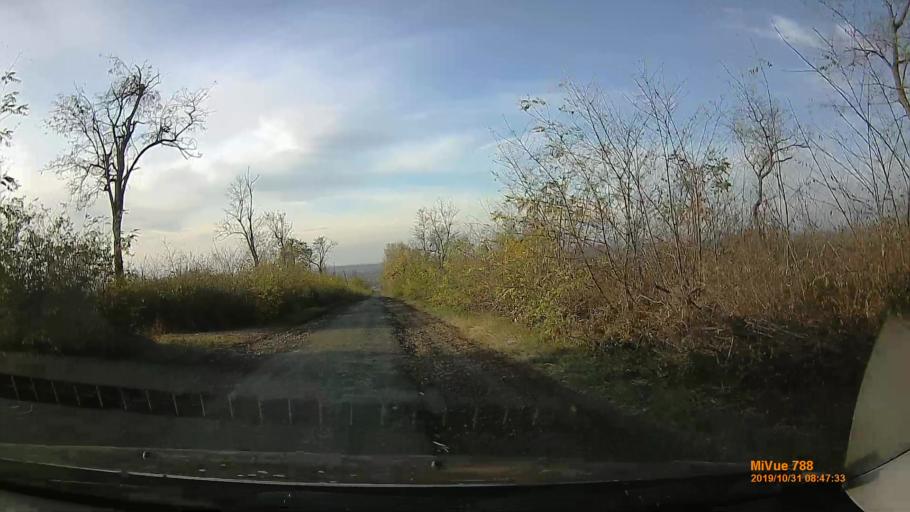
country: HU
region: Pest
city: Albertirsa
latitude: 47.2790
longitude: 19.6084
